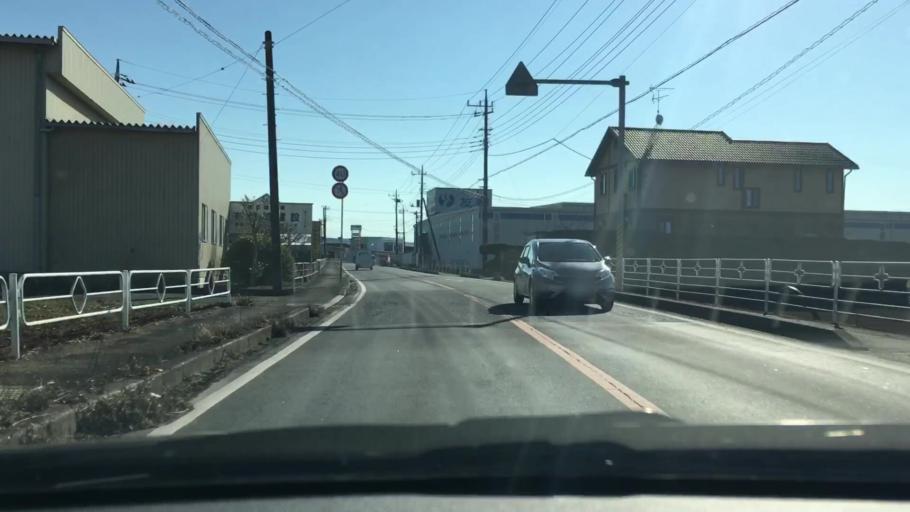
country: JP
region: Chiba
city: Shisui
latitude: 35.7065
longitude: 140.3146
